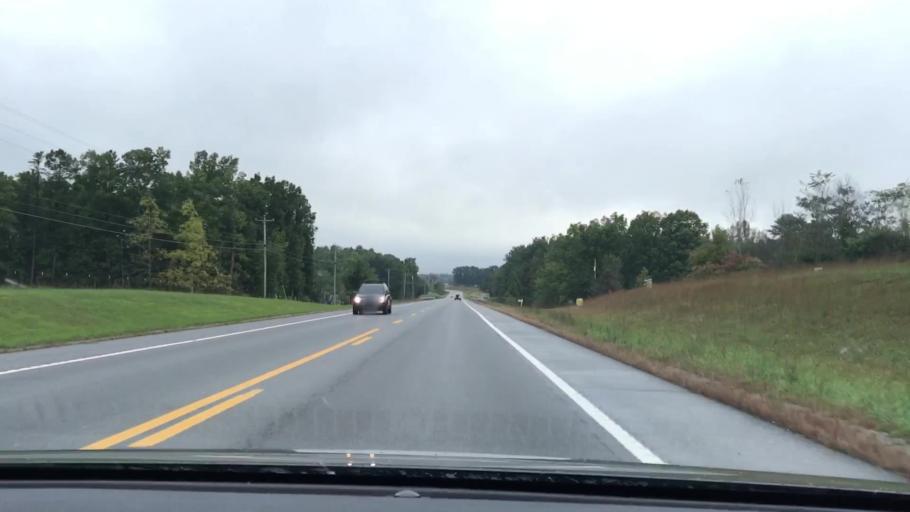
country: US
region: Tennessee
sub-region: Fentress County
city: Grimsley
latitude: 36.2929
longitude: -84.9752
